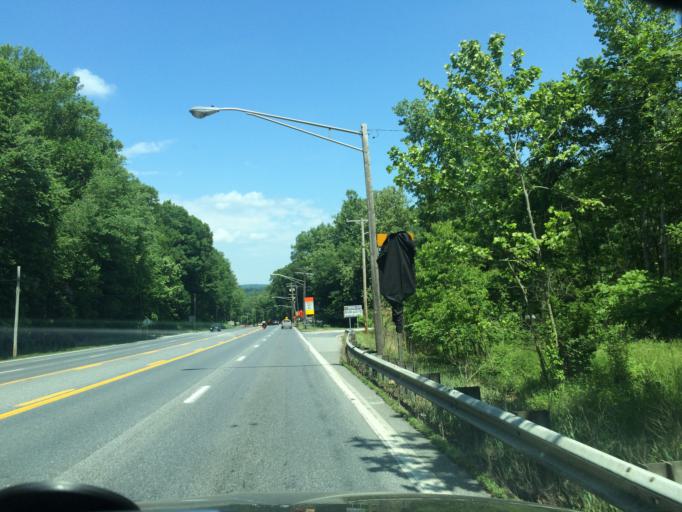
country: US
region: Maryland
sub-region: Baltimore County
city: Reisterstown
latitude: 39.4840
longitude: -76.8590
